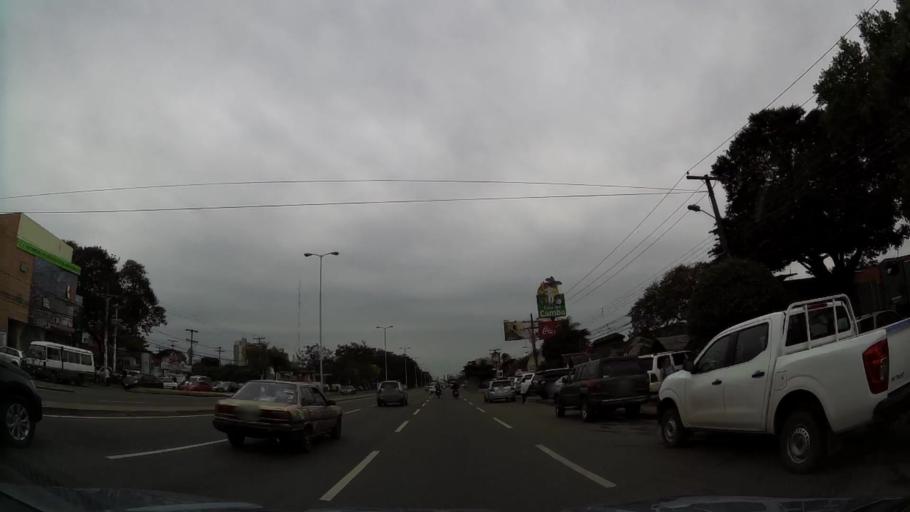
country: BO
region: Santa Cruz
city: Santa Cruz de la Sierra
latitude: -17.7702
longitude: -63.1734
